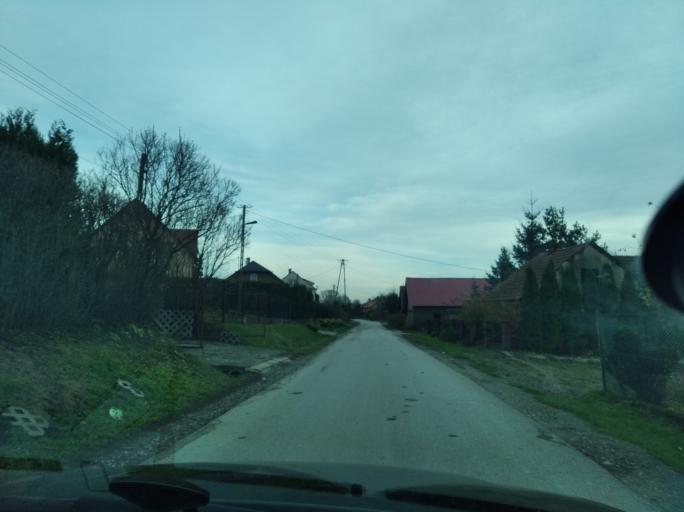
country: PL
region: Subcarpathian Voivodeship
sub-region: Powiat przeworski
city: Debow
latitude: 50.0475
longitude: 22.4430
